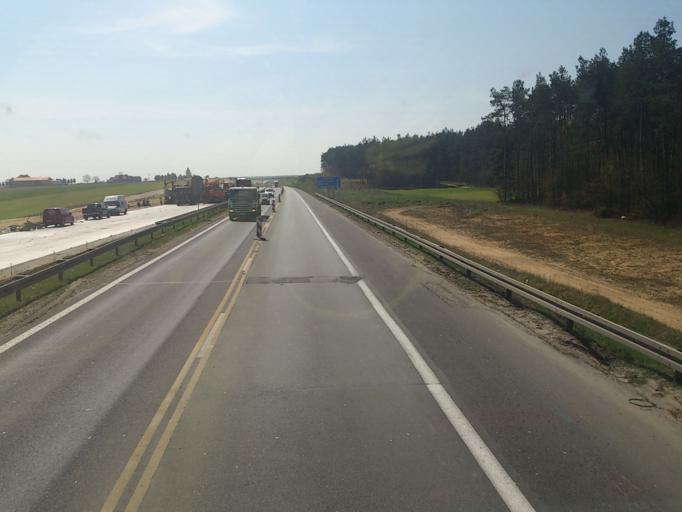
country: PL
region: Lodz Voivodeship
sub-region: Powiat piotrkowski
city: Grabica
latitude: 51.5404
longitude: 19.6018
